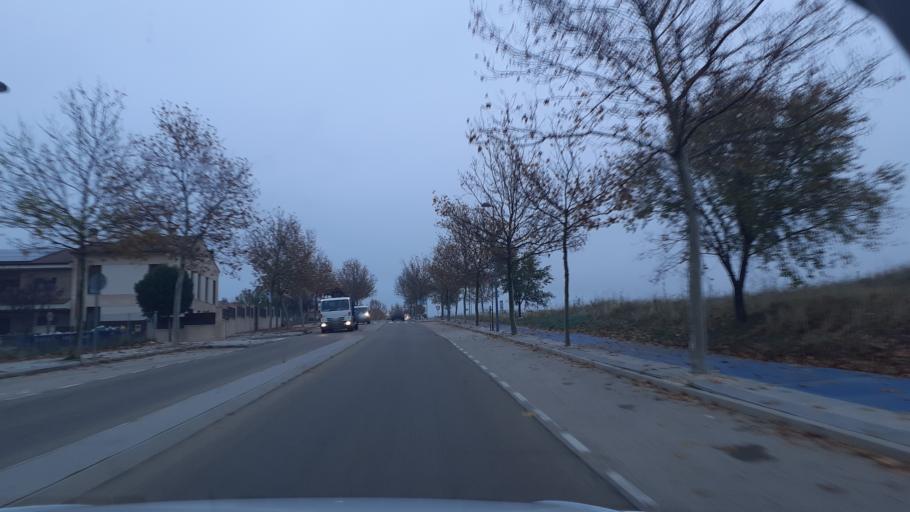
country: ES
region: Madrid
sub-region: Provincia de Madrid
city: Paracuellos de Jarama
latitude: 40.5093
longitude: -3.5121
